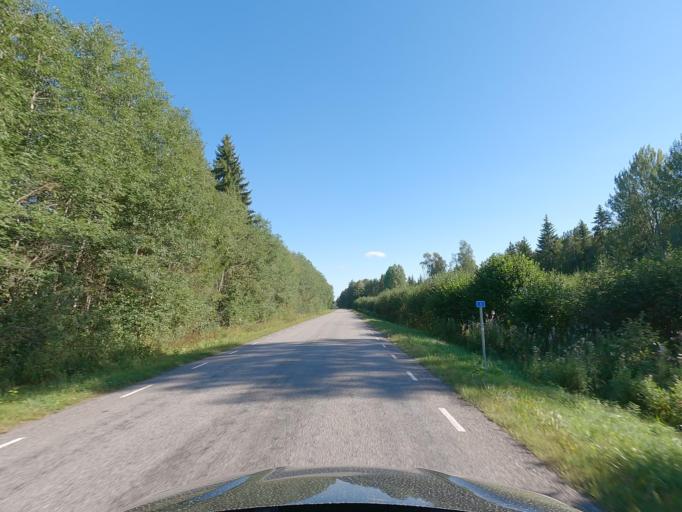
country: EE
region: Raplamaa
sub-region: Kohila vald
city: Kohila
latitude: 59.1336
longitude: 24.6625
